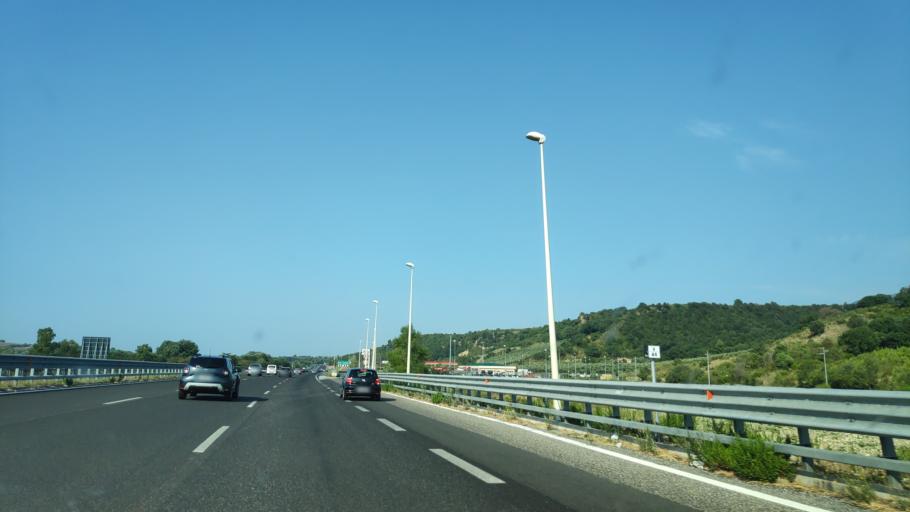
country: IT
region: Campania
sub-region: Provincia di Salerno
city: Serre
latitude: 40.6186
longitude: 15.1688
